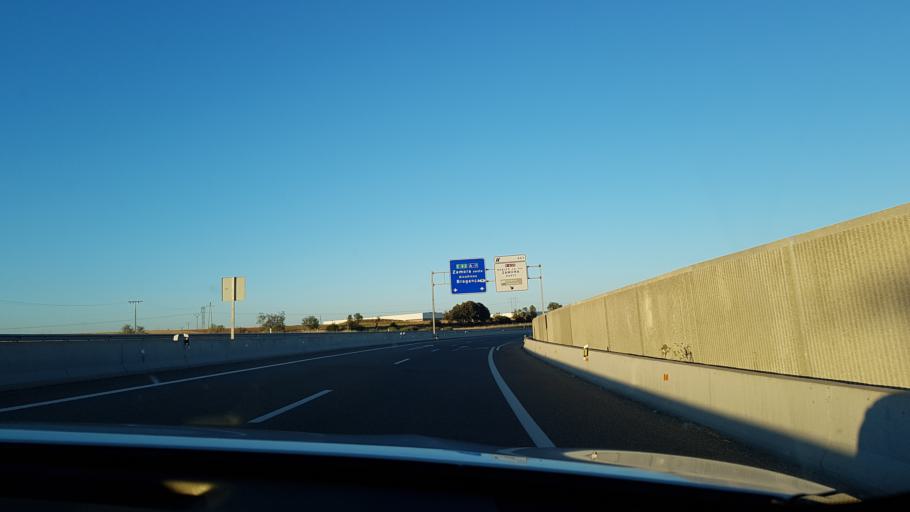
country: ES
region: Castille and Leon
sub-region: Provincia de Zamora
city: Valcabado
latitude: 41.5450
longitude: -5.7583
